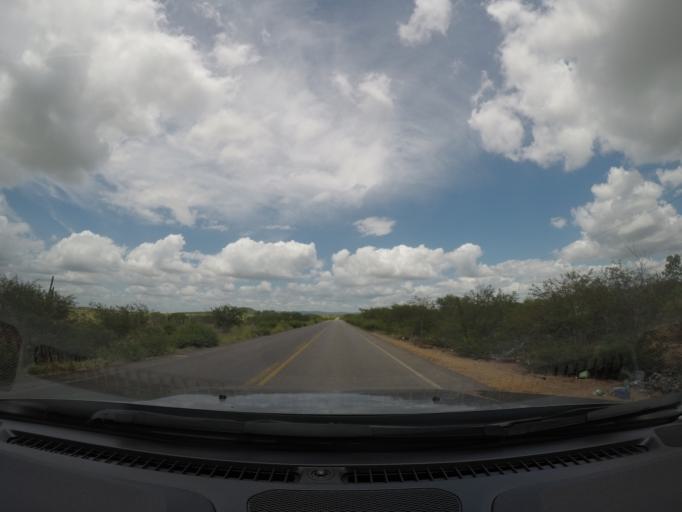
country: BR
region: Bahia
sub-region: Ipira
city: Ipira
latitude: -12.2460
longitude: -39.8076
